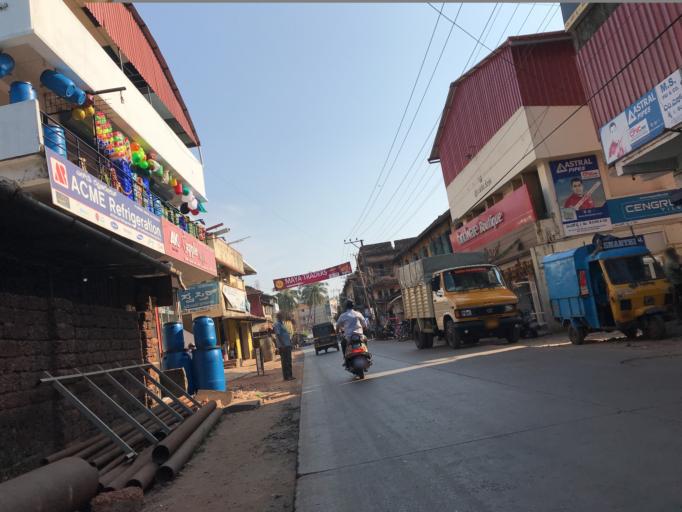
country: IN
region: Karnataka
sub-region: Dakshina Kannada
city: Mangalore
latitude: 12.8657
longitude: 74.8335
